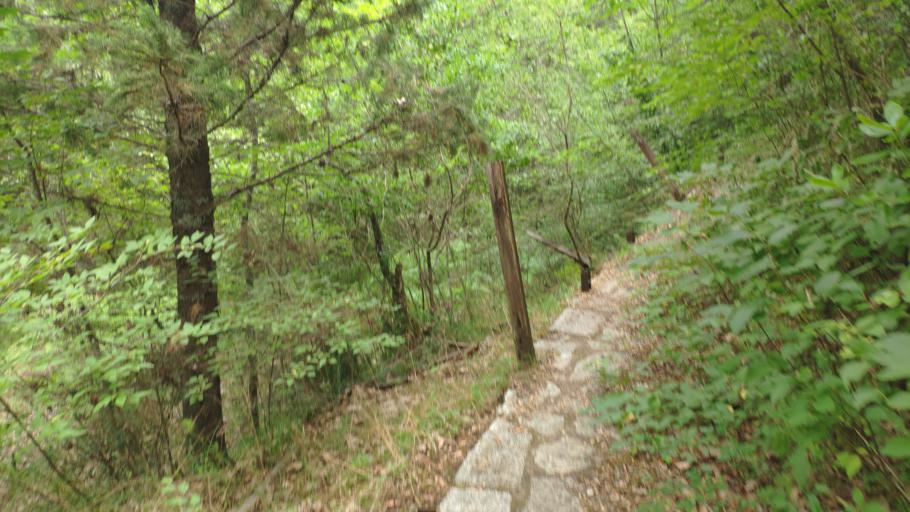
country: GR
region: Ionian Islands
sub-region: Lefkada
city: Lefkada
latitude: 38.8015
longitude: 20.6709
